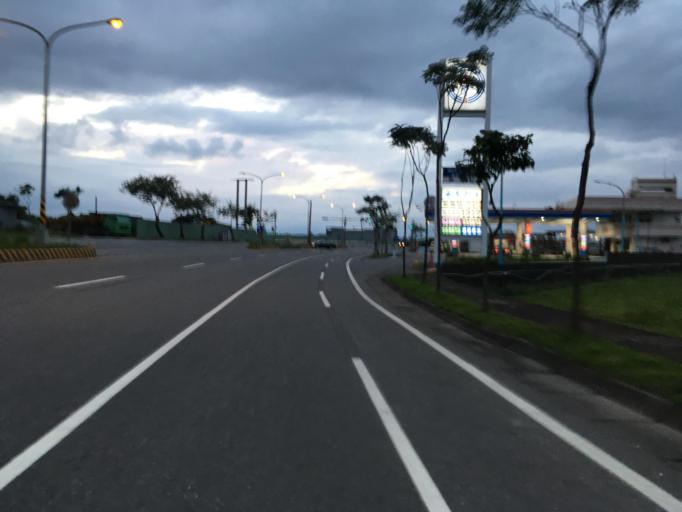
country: TW
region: Taiwan
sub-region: Yilan
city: Yilan
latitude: 24.6270
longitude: 121.8334
